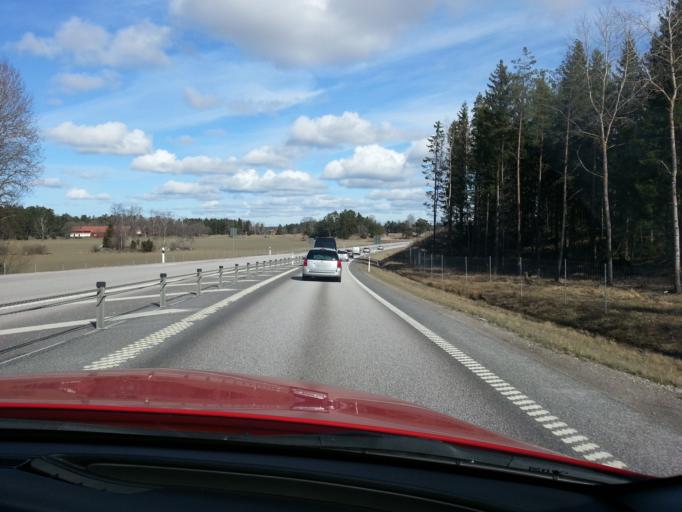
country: SE
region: Uppsala
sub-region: Uppsala Kommun
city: Storvreta
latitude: 59.9325
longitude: 17.8034
